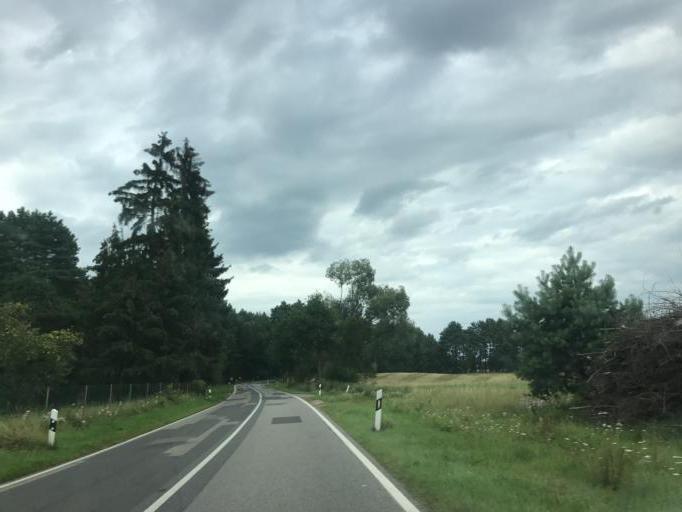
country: DE
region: Mecklenburg-Vorpommern
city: Rechlin
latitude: 53.2554
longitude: 12.7819
